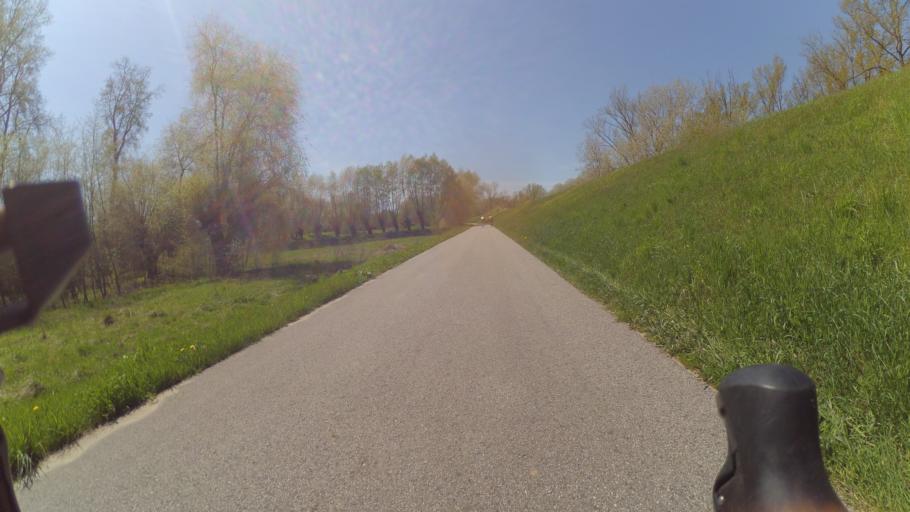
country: PL
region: Masovian Voivodeship
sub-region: Powiat plonski
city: Zaluski
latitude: 52.4192
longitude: 20.5174
